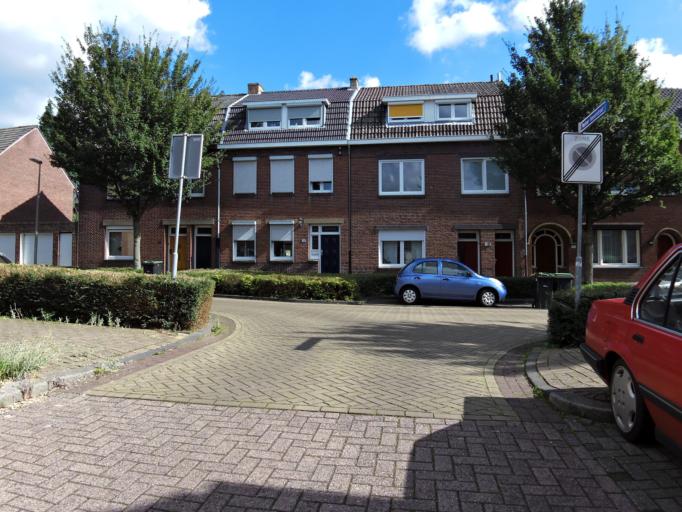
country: NL
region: Limburg
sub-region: Gemeente Kerkrade
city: Kerkrade
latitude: 50.8588
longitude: 6.0309
